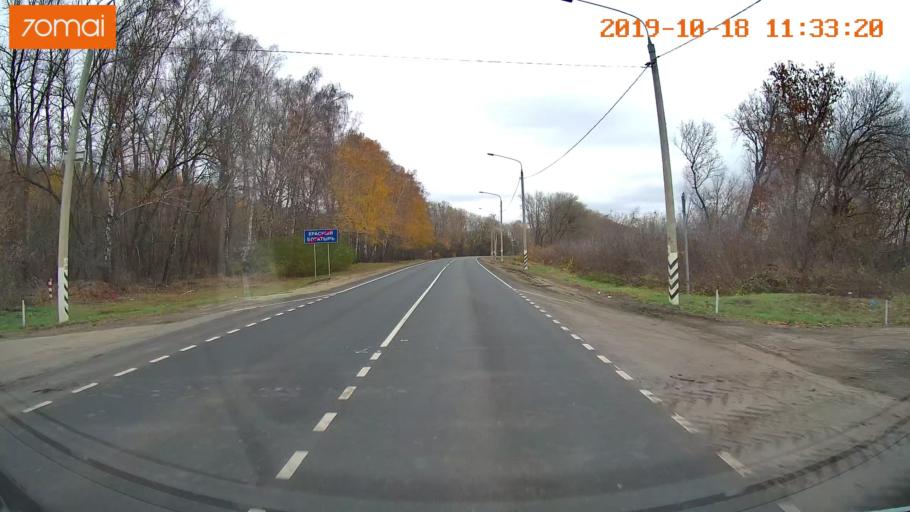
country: RU
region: Rjazan
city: Oktyabr'skiy
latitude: 54.1414
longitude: 38.7378
